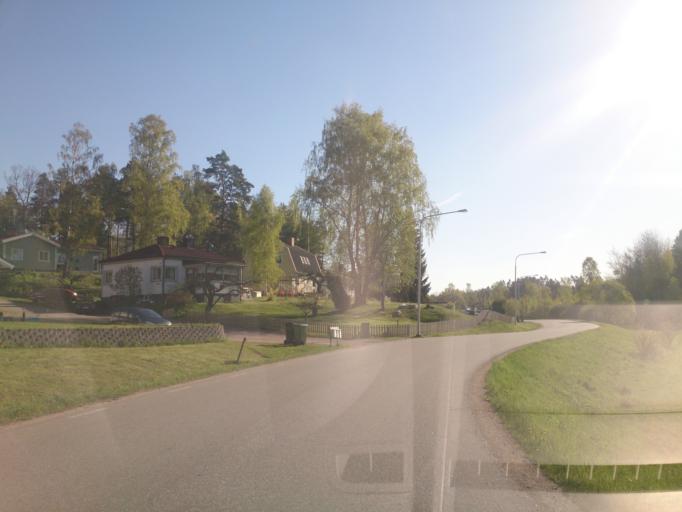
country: SE
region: OEstergoetland
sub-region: Linkopings Kommun
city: Ljungsbro
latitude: 58.5187
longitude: 15.5184
